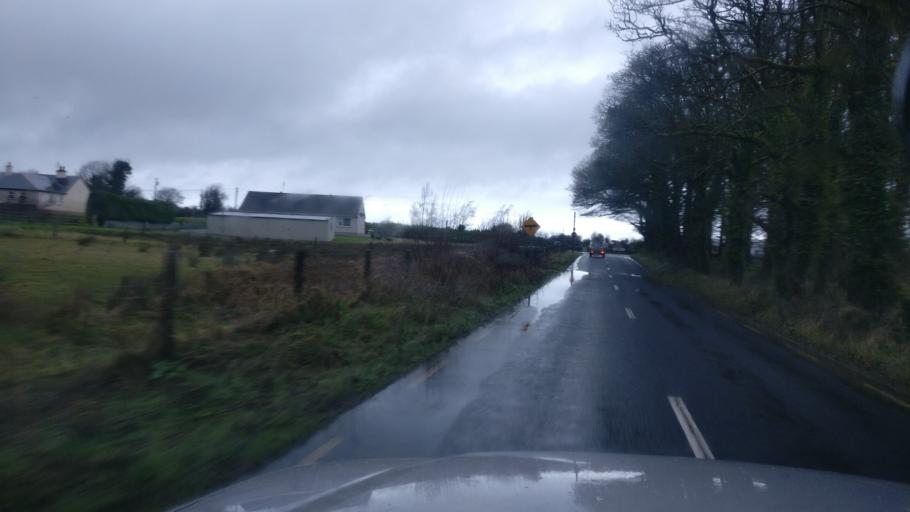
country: IE
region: Connaught
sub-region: County Galway
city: Ballinasloe
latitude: 53.3271
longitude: -8.4066
